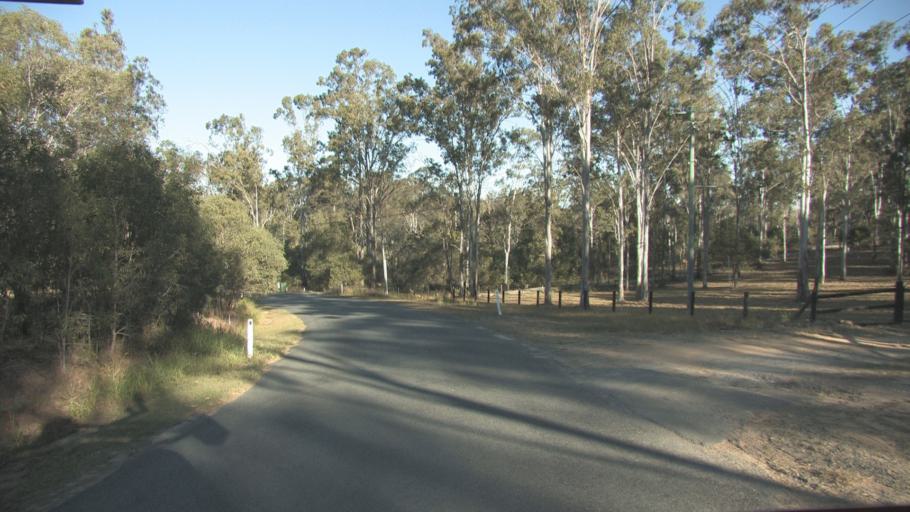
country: AU
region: Queensland
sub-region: Logan
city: North Maclean
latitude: -27.8118
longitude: 153.0411
